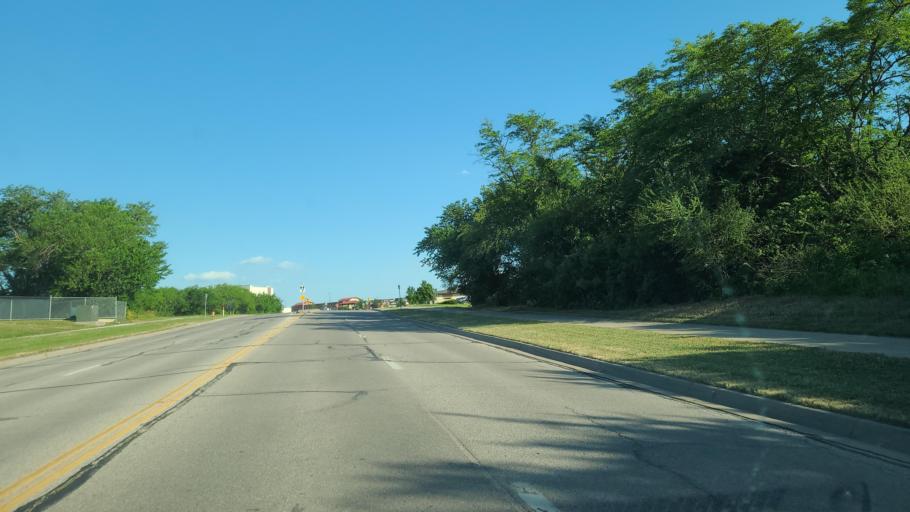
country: US
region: Kansas
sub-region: Douglas County
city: Lawrence
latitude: 38.9757
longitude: -95.3085
